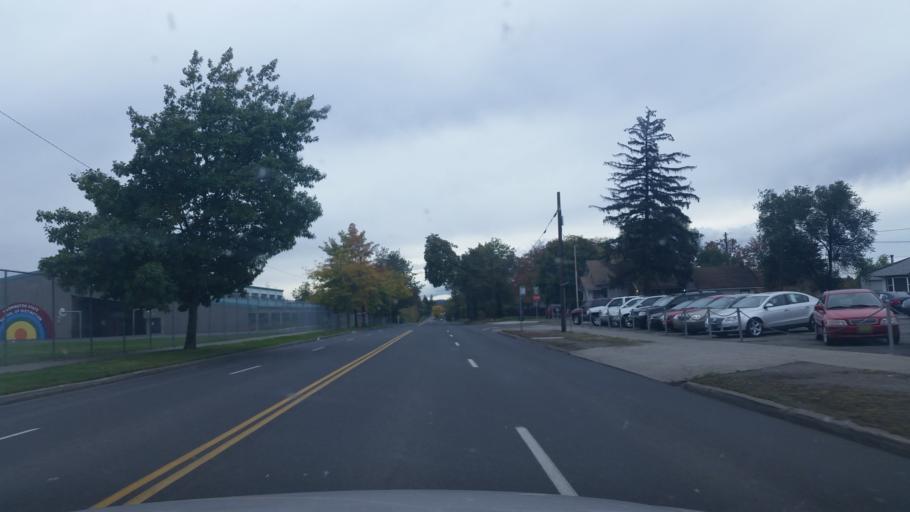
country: US
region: Washington
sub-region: Spokane County
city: Spokane
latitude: 47.6718
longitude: -117.3828
